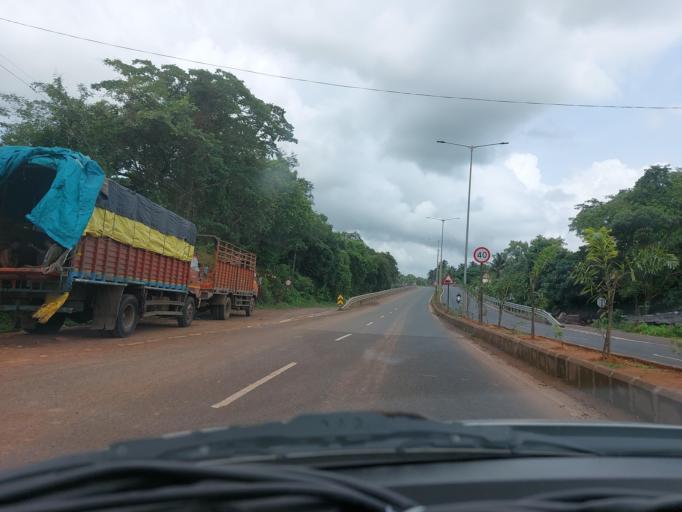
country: IN
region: Goa
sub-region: North Goa
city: Queula
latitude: 15.3836
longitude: 74.0027
